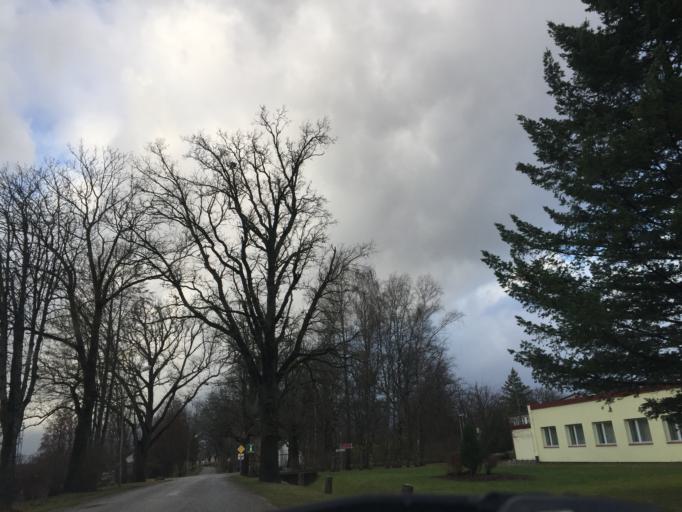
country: LV
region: Burtnieki
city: Matisi
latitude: 57.6943
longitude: 25.2760
